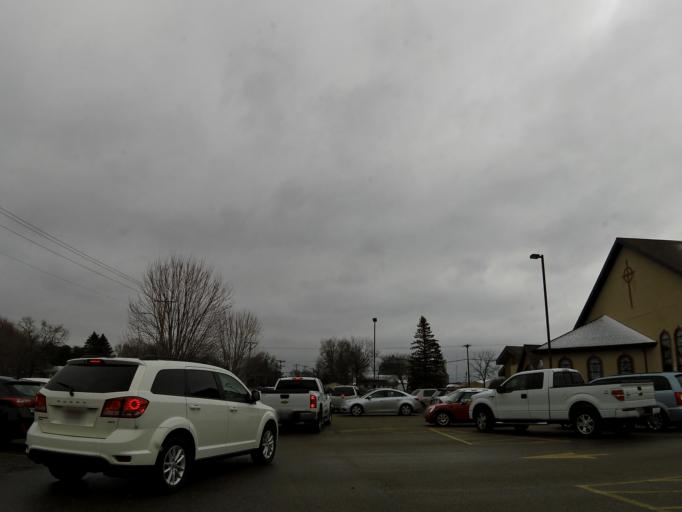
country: US
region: Minnesota
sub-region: Olmsted County
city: Byron
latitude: 44.0325
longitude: -92.6497
